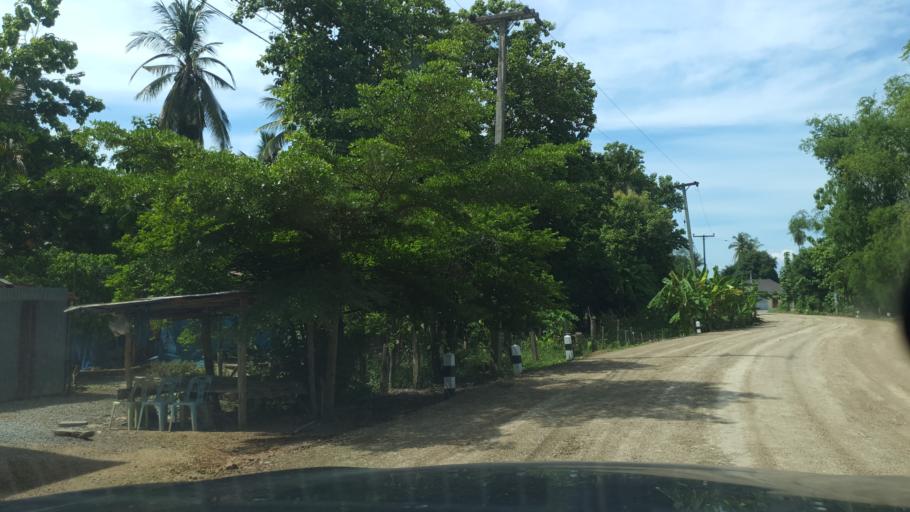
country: TH
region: Sukhothai
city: Si Samrong
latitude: 17.2124
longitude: 99.7189
